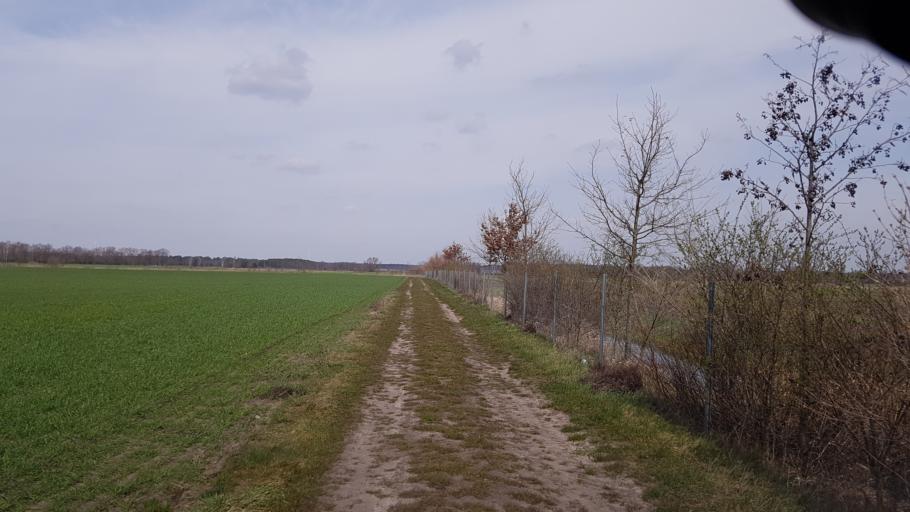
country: DE
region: Brandenburg
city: Bronkow
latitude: 51.6357
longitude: 13.9200
